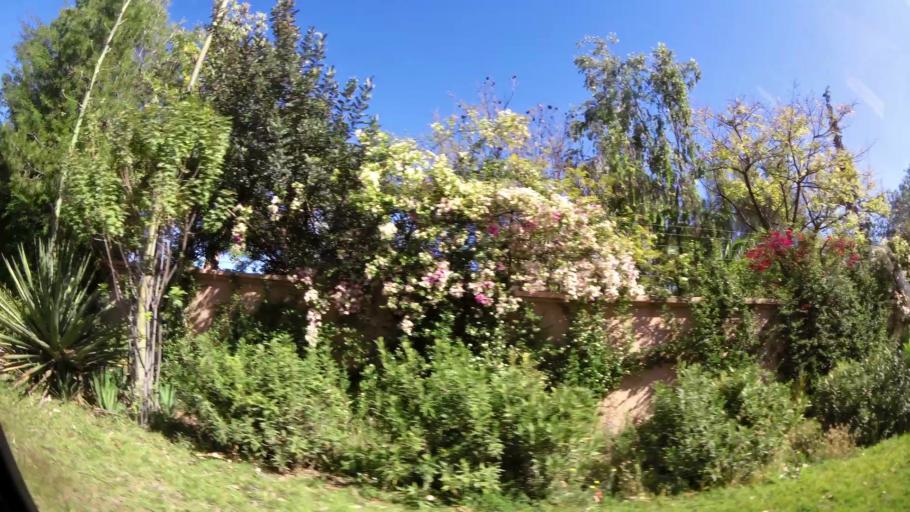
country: MA
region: Marrakech-Tensift-Al Haouz
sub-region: Marrakech
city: Marrakesh
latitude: 31.6629
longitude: -7.9371
